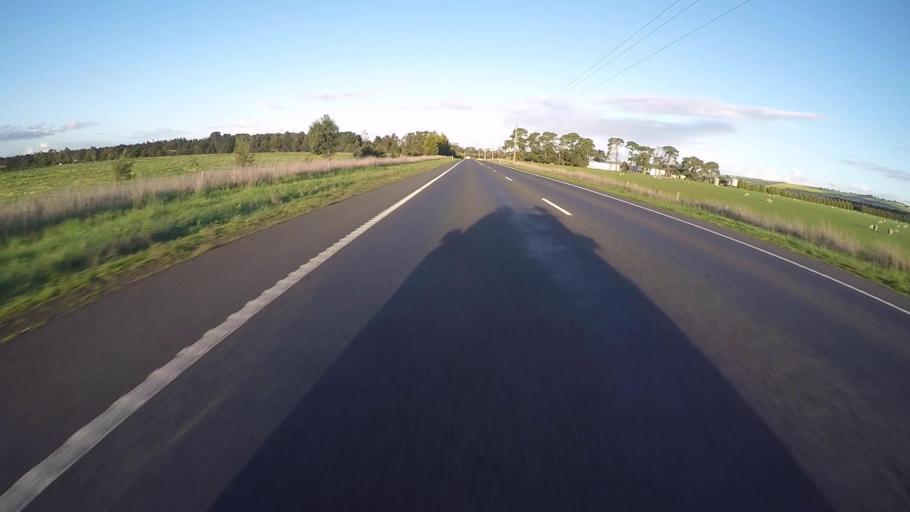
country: AU
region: Victoria
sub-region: Greater Geelong
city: Wandana Heights
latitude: -38.1277
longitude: 144.2531
